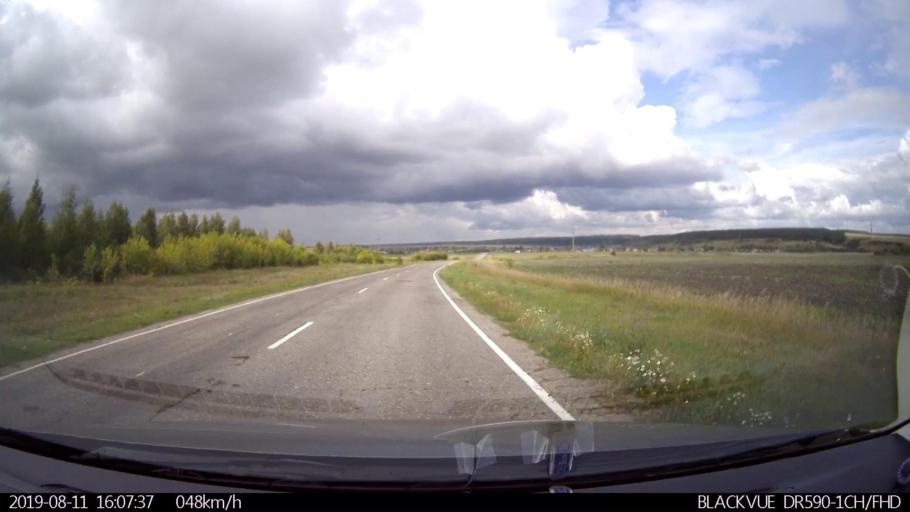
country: RU
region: Ulyanovsk
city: Ignatovka
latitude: 53.9785
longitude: 47.6465
